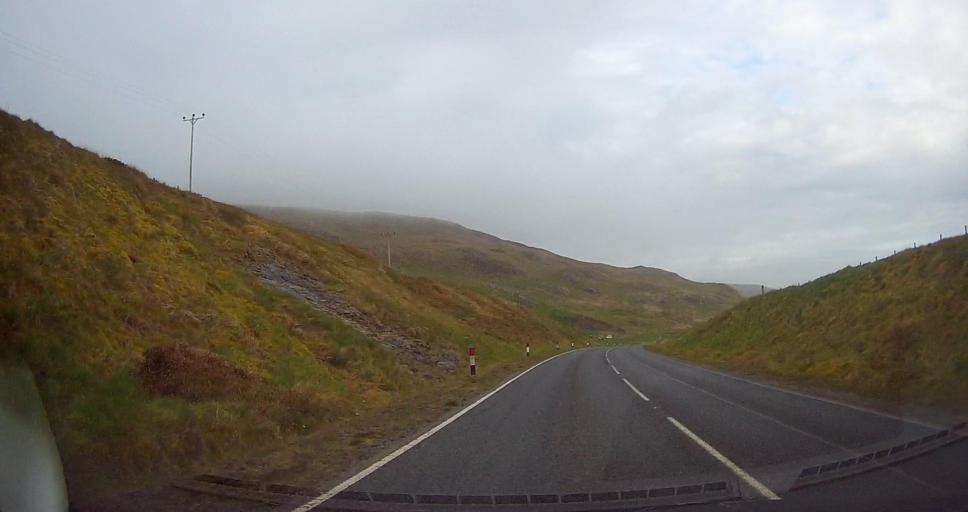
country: GB
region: Scotland
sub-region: Shetland Islands
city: Sandwick
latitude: 60.0234
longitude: -1.2359
